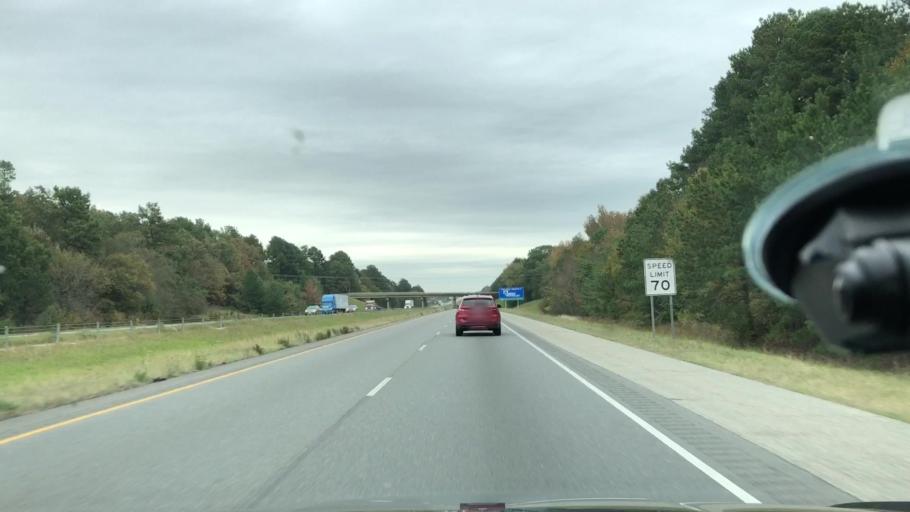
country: US
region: Arkansas
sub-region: Miller County
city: Texarkana
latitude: 33.4857
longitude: -93.9758
